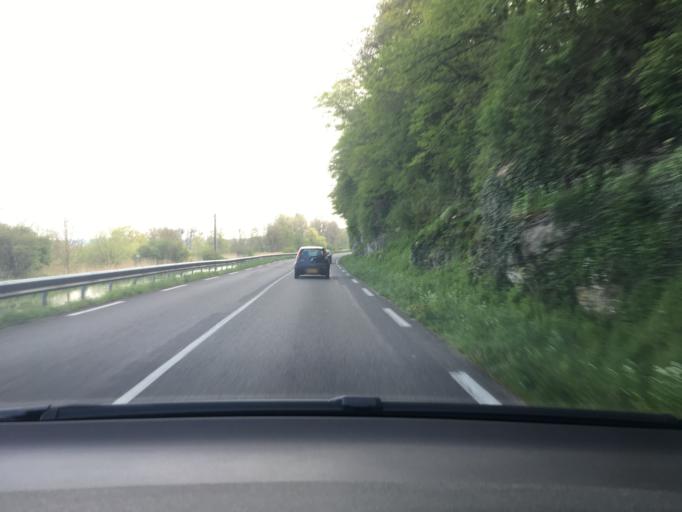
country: FR
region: Franche-Comte
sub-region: Departement du Doubs
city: Bart
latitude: 47.4846
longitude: 6.7715
